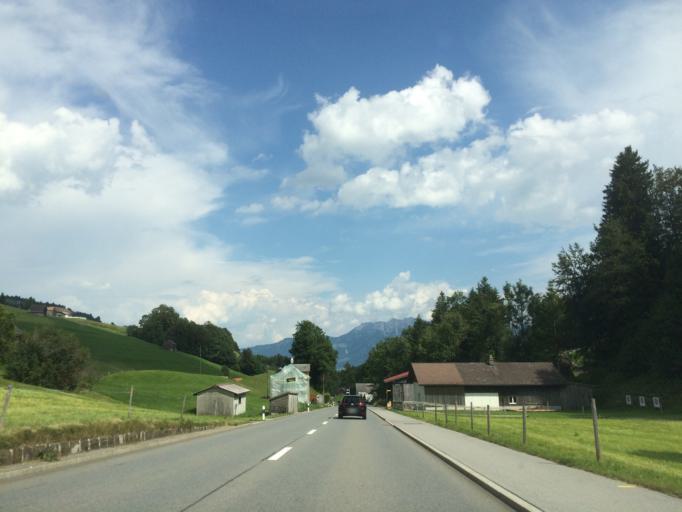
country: CH
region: Saint Gallen
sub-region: Wahlkreis Toggenburg
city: Wildhaus
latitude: 47.1991
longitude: 9.3676
